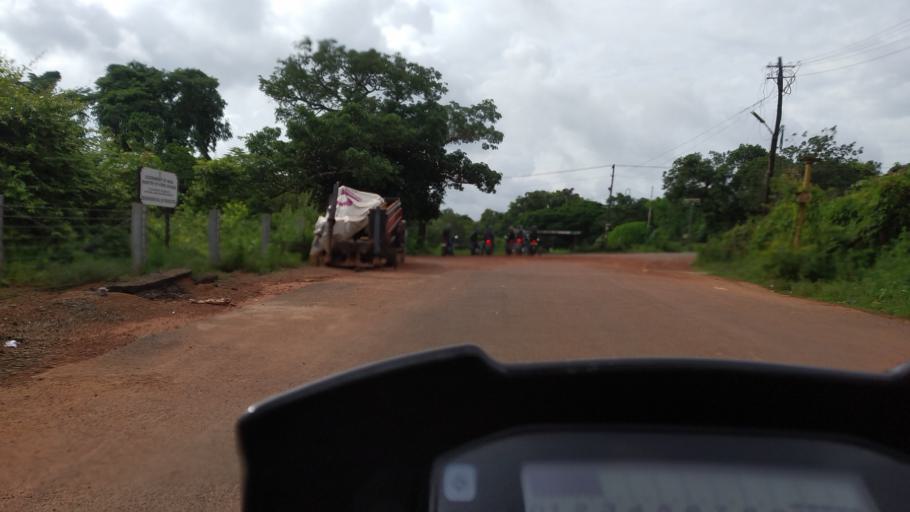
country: IN
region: Kerala
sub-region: Ernakulam
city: Aluva
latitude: 10.0504
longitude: 76.3455
